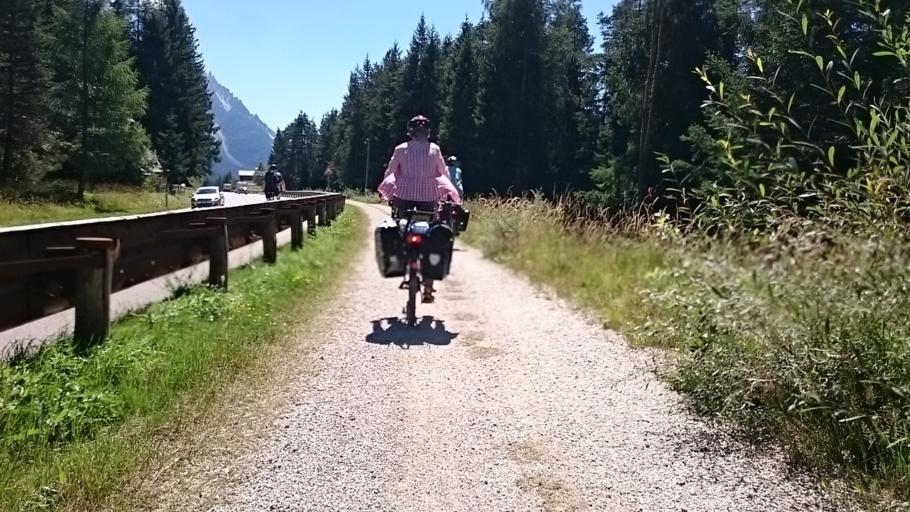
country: IT
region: Veneto
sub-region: Provincia di Belluno
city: San Vito
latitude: 46.4931
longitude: 12.1801
